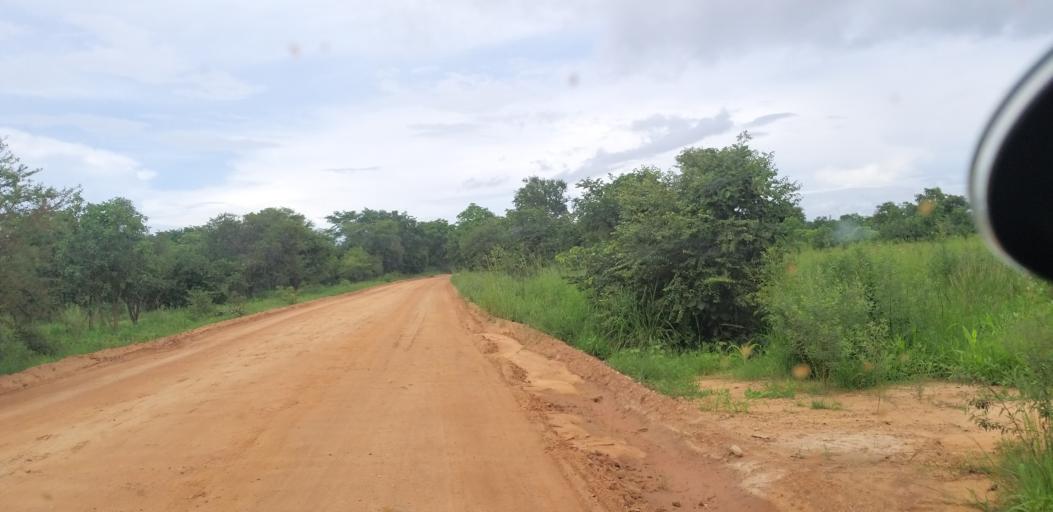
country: ZM
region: Lusaka
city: Lusaka
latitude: -15.1900
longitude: 28.4453
